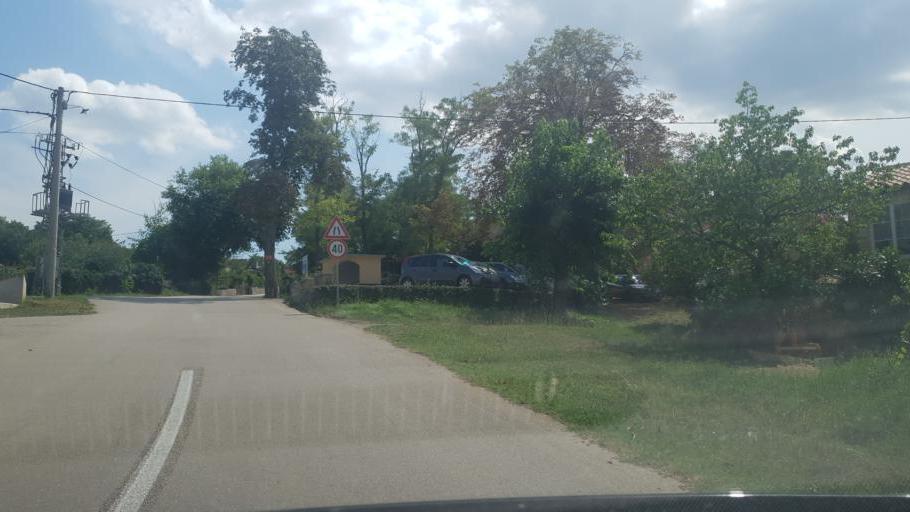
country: HR
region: Primorsko-Goranska
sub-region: Grad Crikvenica
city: Crikvenica
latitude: 45.1359
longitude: 14.6218
